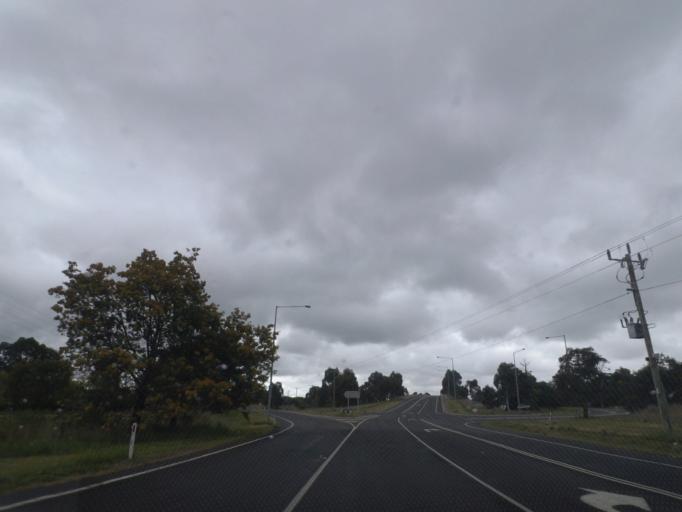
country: AU
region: Victoria
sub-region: Hume
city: Sunbury
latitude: -37.3229
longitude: 144.5241
